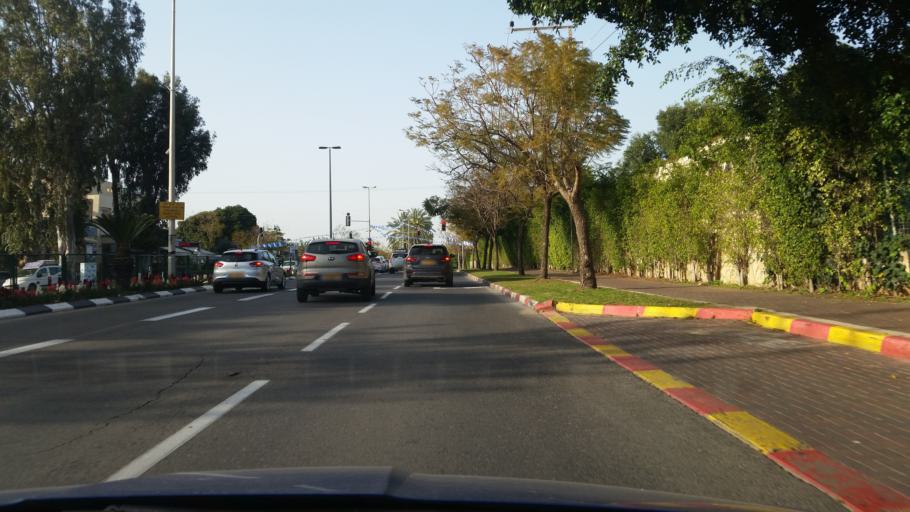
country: IL
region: Central District
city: Ra'anana
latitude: 32.1890
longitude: 34.8550
